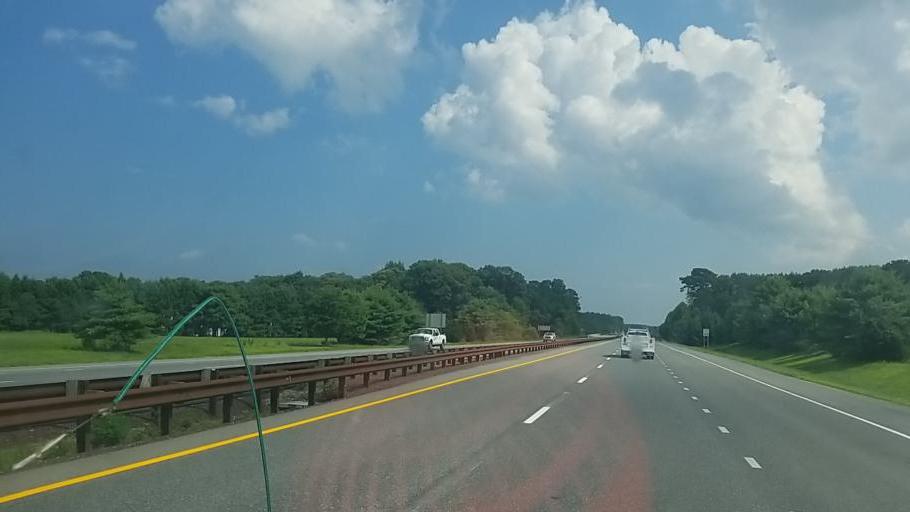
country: US
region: Maryland
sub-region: Worcester County
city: Ocean Pines
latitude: 38.4036
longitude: -75.2113
